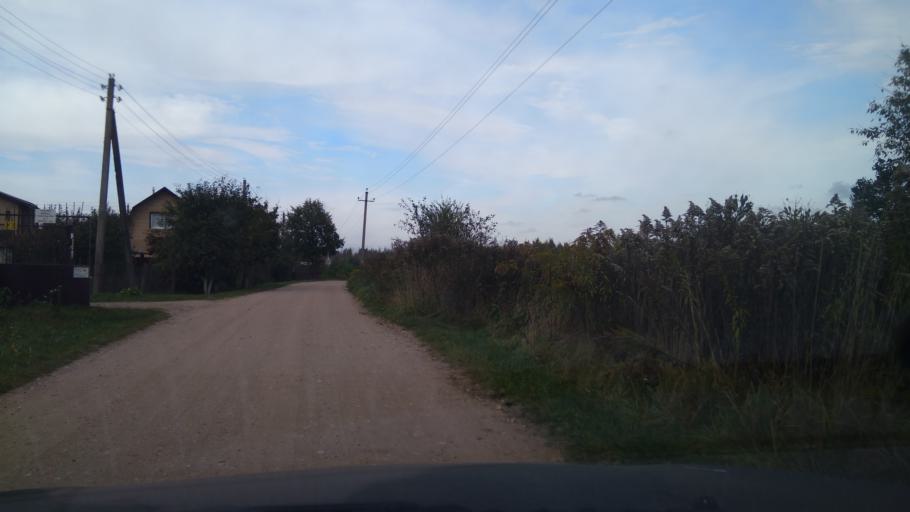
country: BY
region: Minsk
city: Rudzyensk
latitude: 53.6076
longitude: 27.8483
